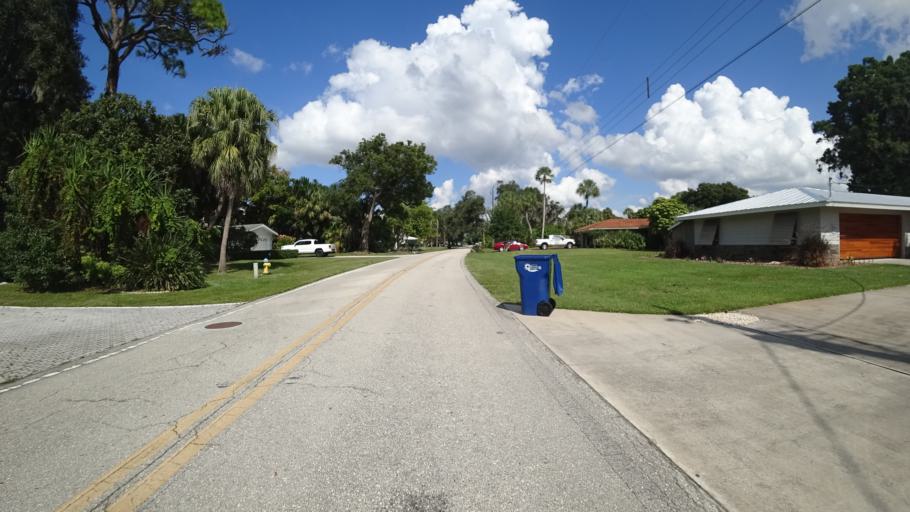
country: US
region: Florida
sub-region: Manatee County
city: Whitfield
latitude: 27.4205
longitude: -82.5644
